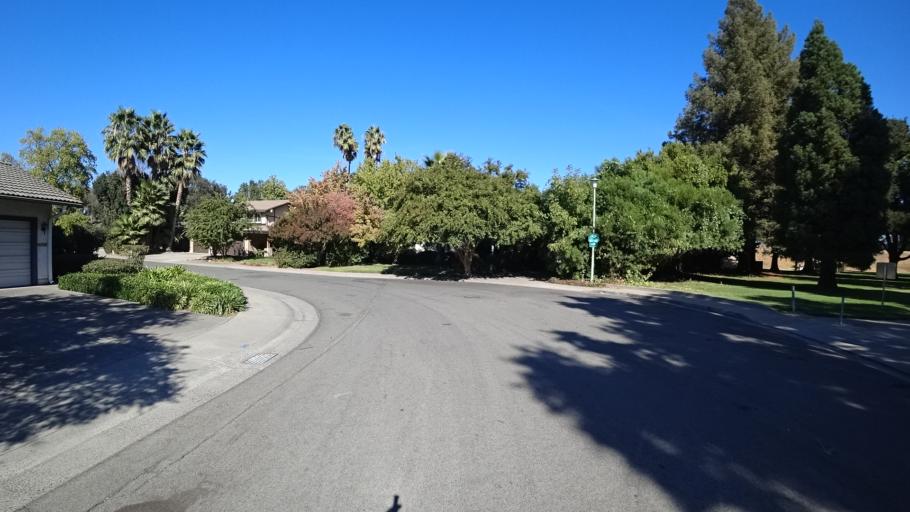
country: US
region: California
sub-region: Yolo County
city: West Sacramento
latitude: 38.5157
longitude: -121.5313
